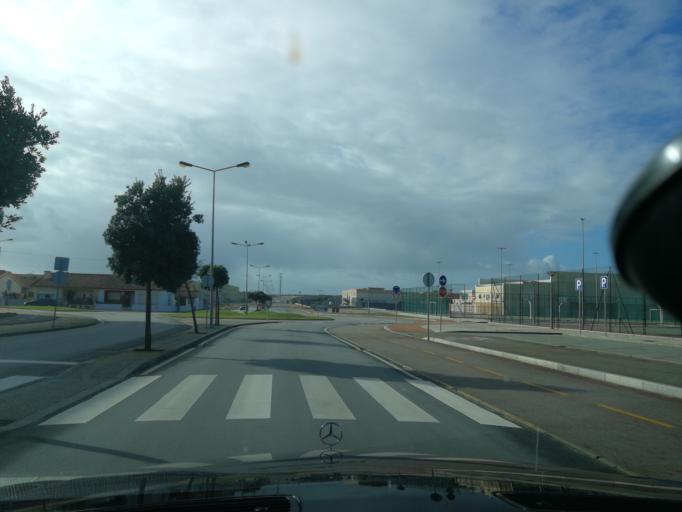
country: PT
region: Aveiro
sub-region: Murtosa
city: Murtosa
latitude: 40.7645
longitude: -8.7041
